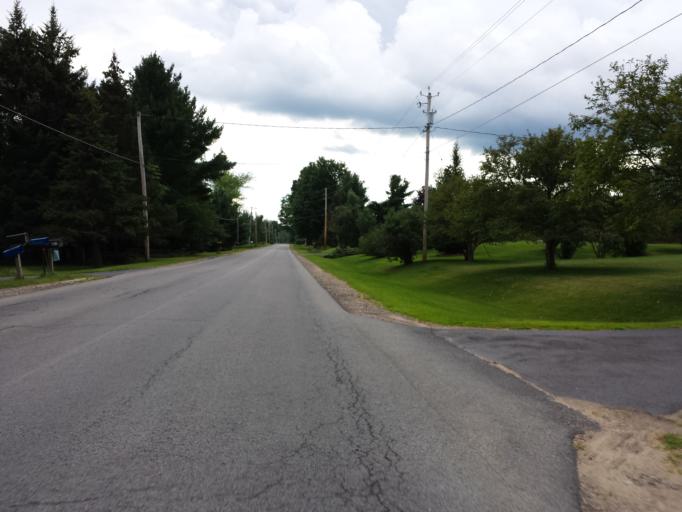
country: US
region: New York
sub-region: St. Lawrence County
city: Potsdam
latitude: 44.6974
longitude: -75.0125
